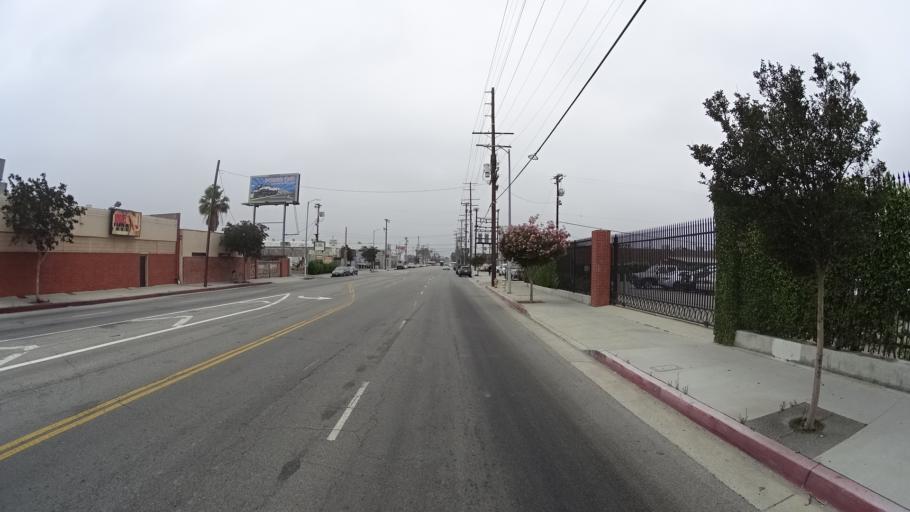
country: US
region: California
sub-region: Los Angeles County
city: Van Nuys
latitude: 34.2044
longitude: -118.4139
